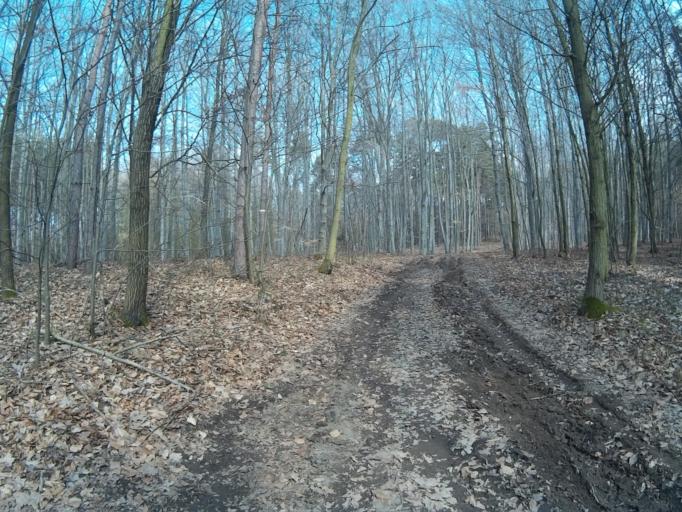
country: CZ
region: South Moravian
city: Vinicne Sumice
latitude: 49.2166
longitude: 16.8125
